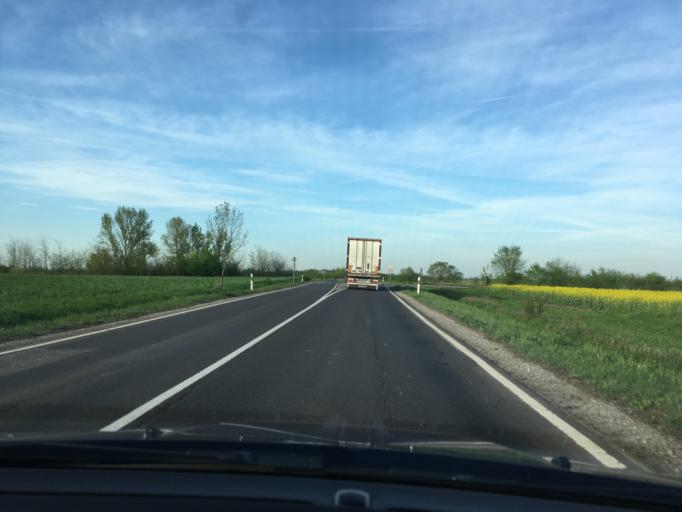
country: HU
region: Hajdu-Bihar
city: Berettyoujfalu
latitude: 47.1665
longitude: 21.5123
